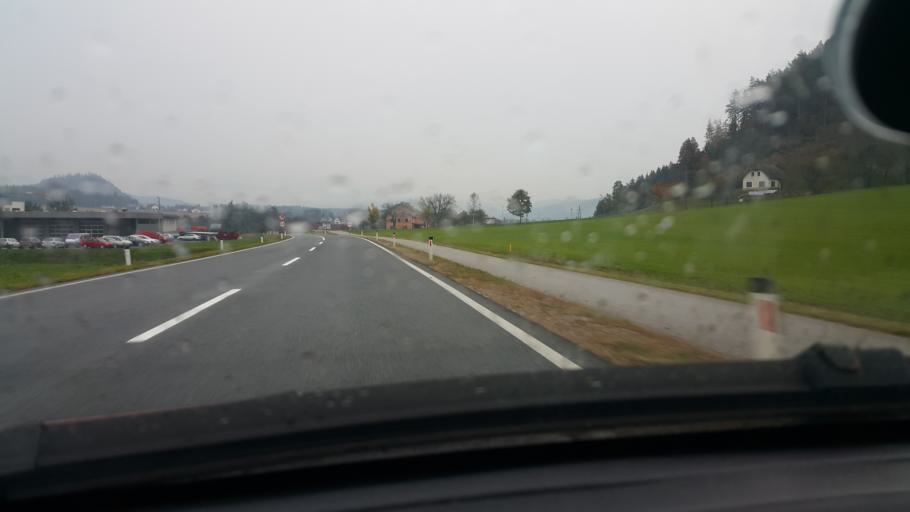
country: AT
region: Carinthia
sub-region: Politischer Bezirk Volkermarkt
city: Ruden
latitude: 46.6476
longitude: 14.7716
